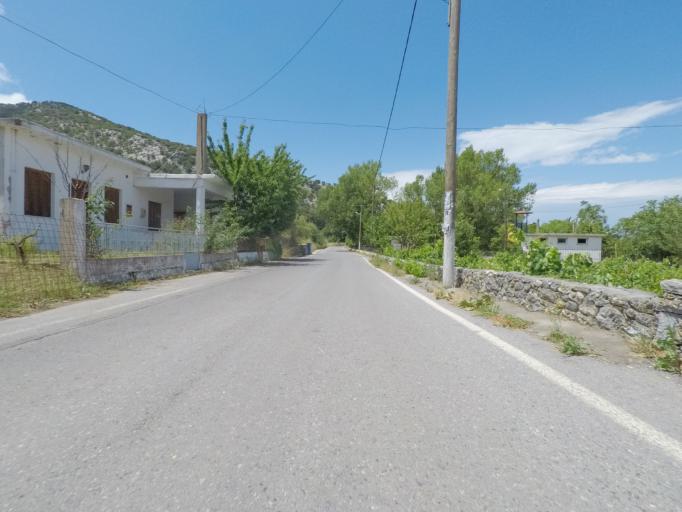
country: GR
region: Crete
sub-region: Nomos Irakleiou
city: Mokhos
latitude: 35.1709
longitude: 25.4378
